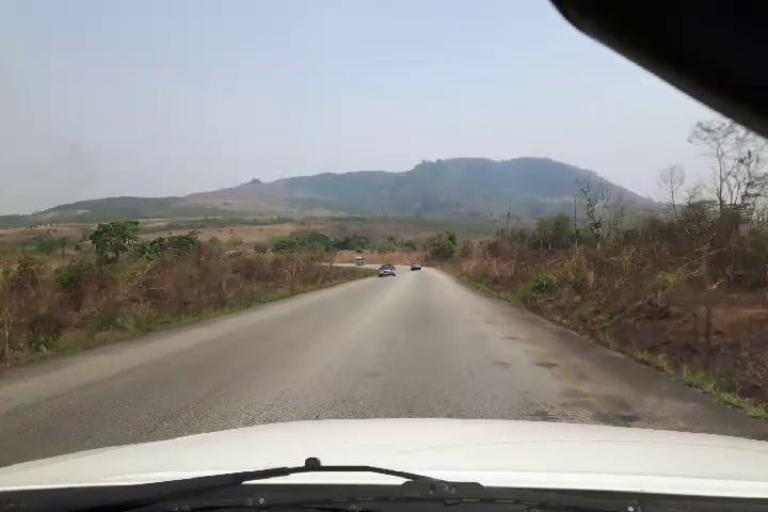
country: SL
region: Northern Province
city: Yonibana
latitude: 8.3871
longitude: -12.1919
